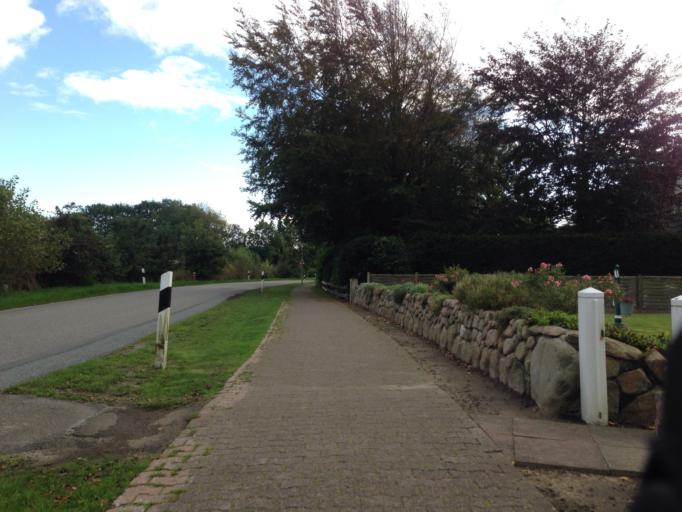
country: DE
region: Schleswig-Holstein
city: Suderende
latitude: 54.7203
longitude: 8.4363
